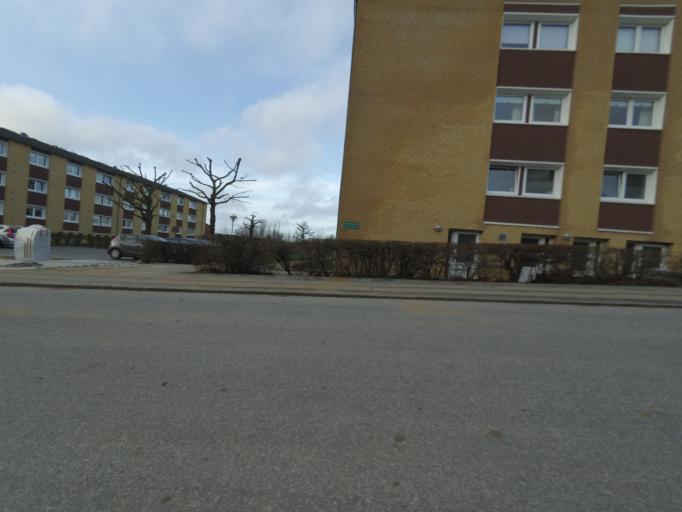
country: DK
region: Central Jutland
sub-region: Arhus Kommune
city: Arhus
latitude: 56.1223
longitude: 10.1750
